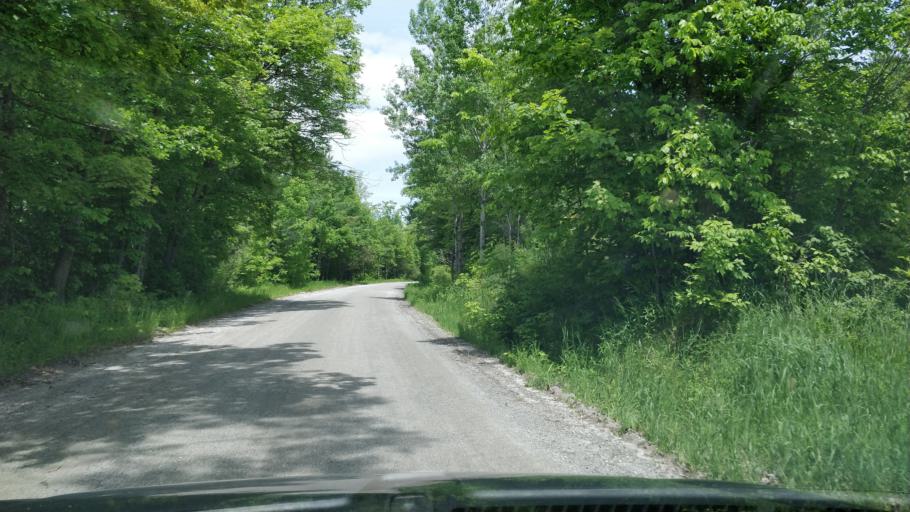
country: CA
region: Ontario
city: Perth
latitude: 44.7298
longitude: -76.5075
